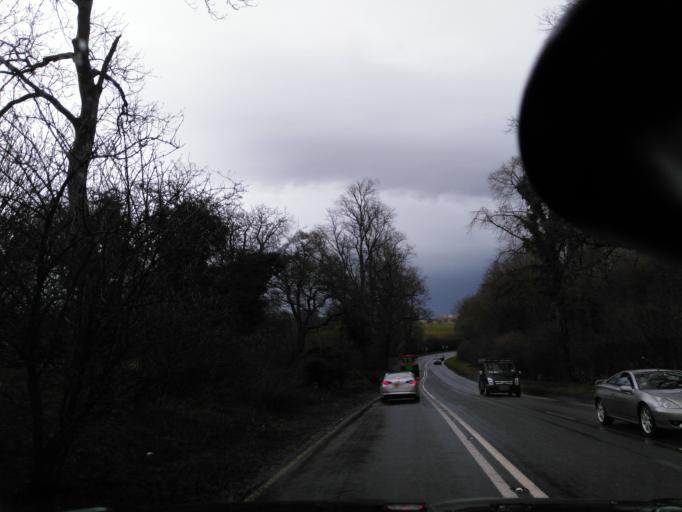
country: GB
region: England
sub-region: North Yorkshire
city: Harrogate
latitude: 54.0606
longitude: -1.5377
